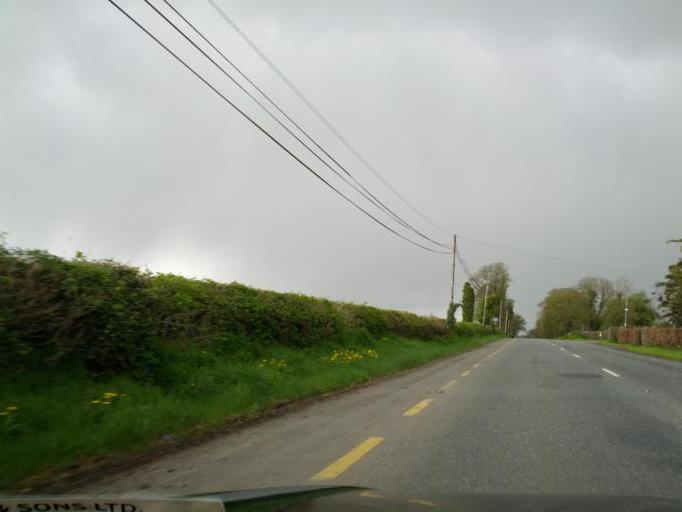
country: IE
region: Leinster
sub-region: An Mhi
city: Dunshaughlin
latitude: 53.5593
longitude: -6.5775
